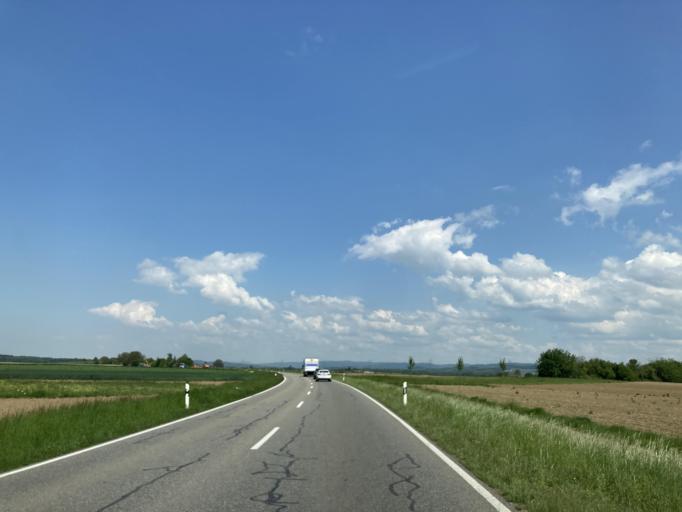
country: DE
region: Baden-Wuerttemberg
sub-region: Freiburg Region
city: Endingen
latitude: 48.1528
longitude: 7.7095
